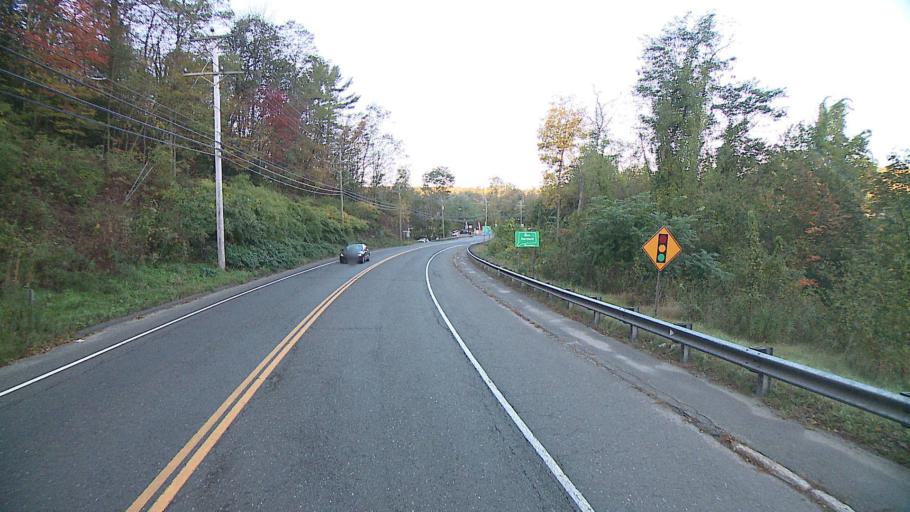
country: US
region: Connecticut
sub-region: Litchfield County
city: New Hartford Center
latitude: 41.8775
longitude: -72.9761
